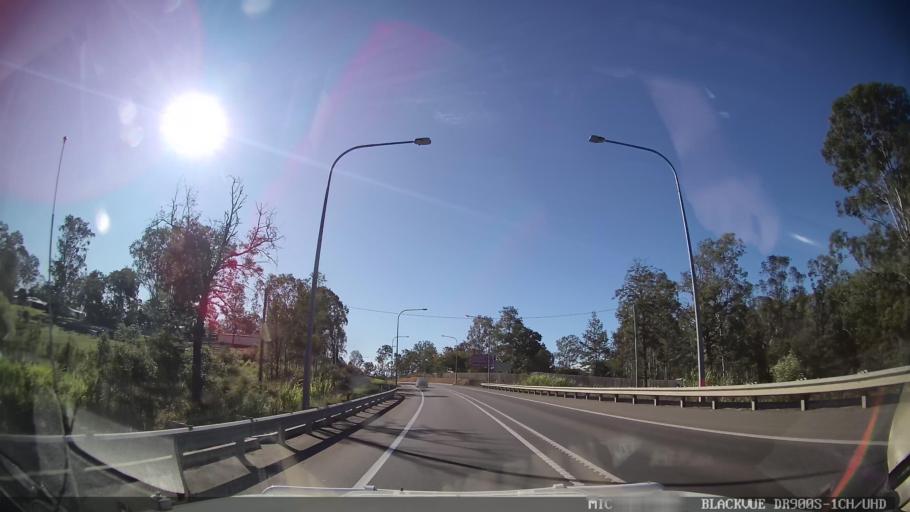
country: AU
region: Queensland
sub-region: Bundaberg
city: Sharon
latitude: -24.9974
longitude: 151.9608
